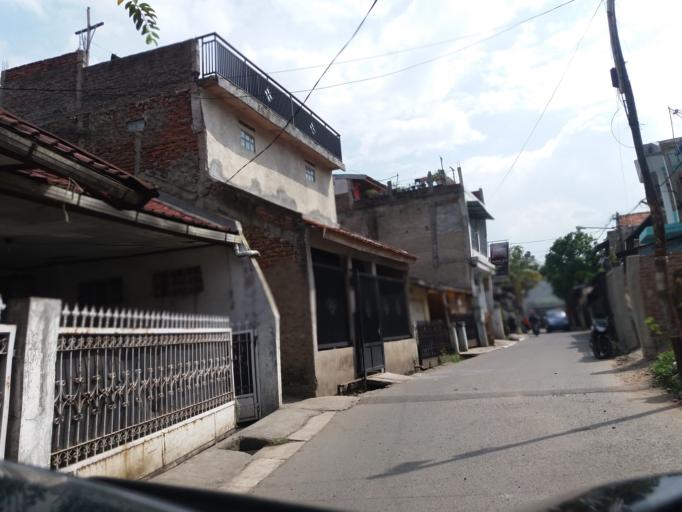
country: ID
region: West Java
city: Bandung
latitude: -6.9256
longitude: 107.6574
